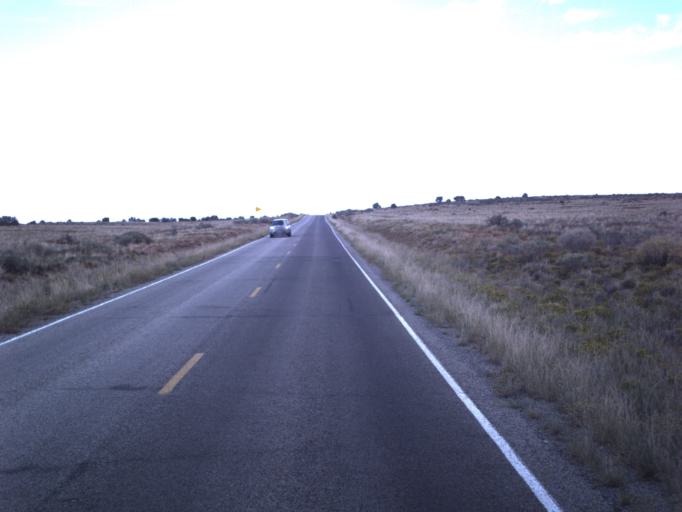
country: US
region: Utah
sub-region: Grand County
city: Moab
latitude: 38.4994
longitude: -109.7327
